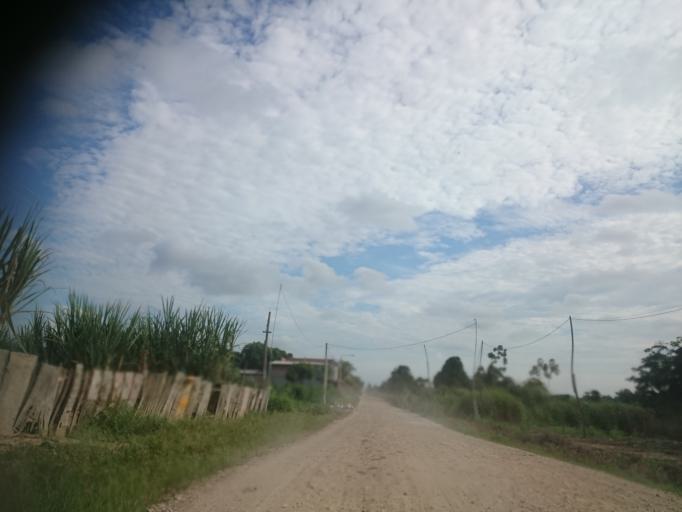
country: PE
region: Ucayali
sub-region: Provincia de Coronel Portillo
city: Puerto Callao
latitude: -8.3733
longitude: -74.5996
